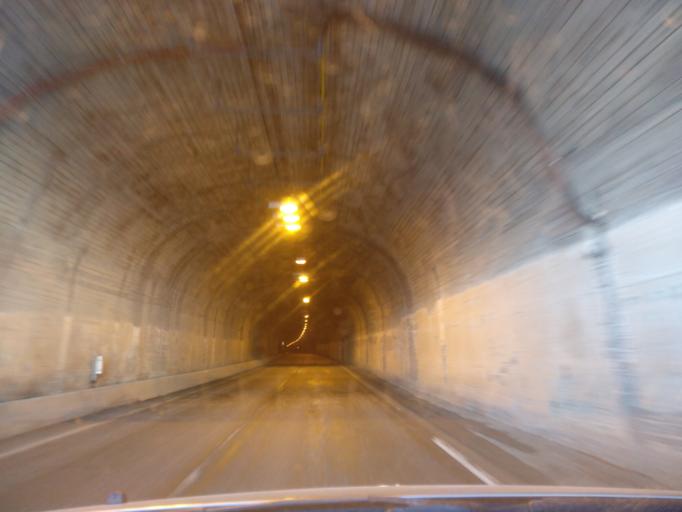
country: NO
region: Aust-Agder
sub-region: Bykle
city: Hovden
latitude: 59.8489
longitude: 7.0850
